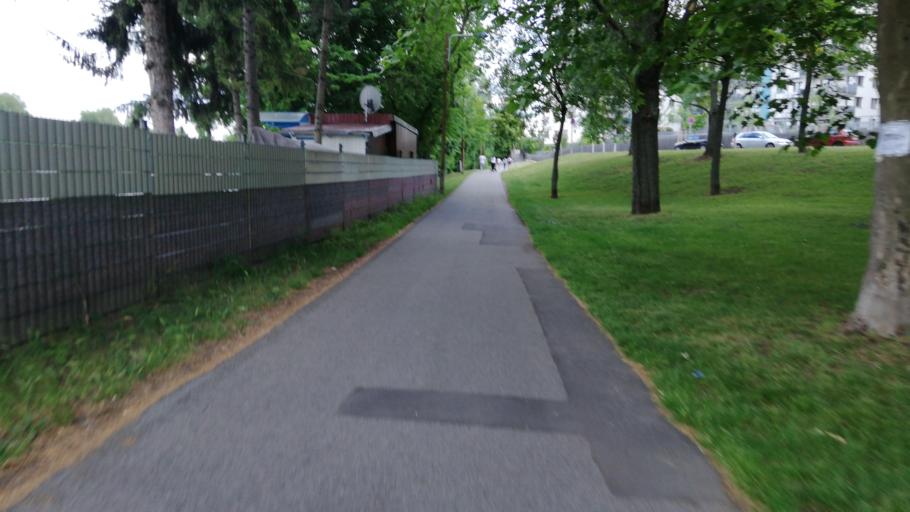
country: AT
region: Vienna
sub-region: Wien Stadt
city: Vienna
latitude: 48.2222
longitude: 16.4279
